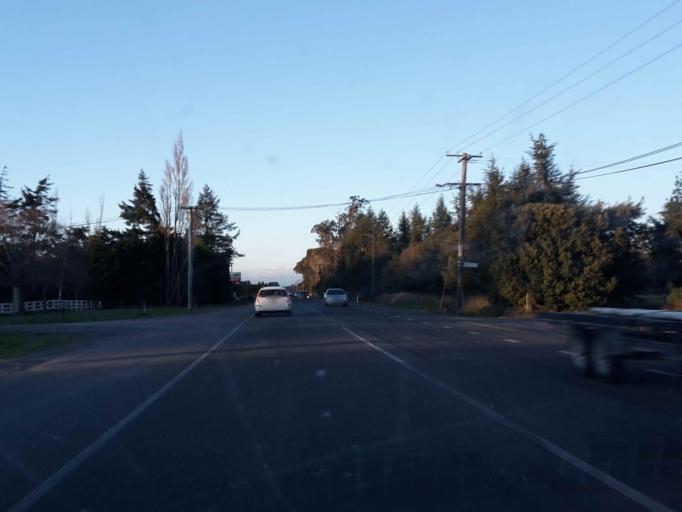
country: NZ
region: Canterbury
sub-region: Selwyn District
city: Rolleston
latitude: -43.5751
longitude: 172.4264
